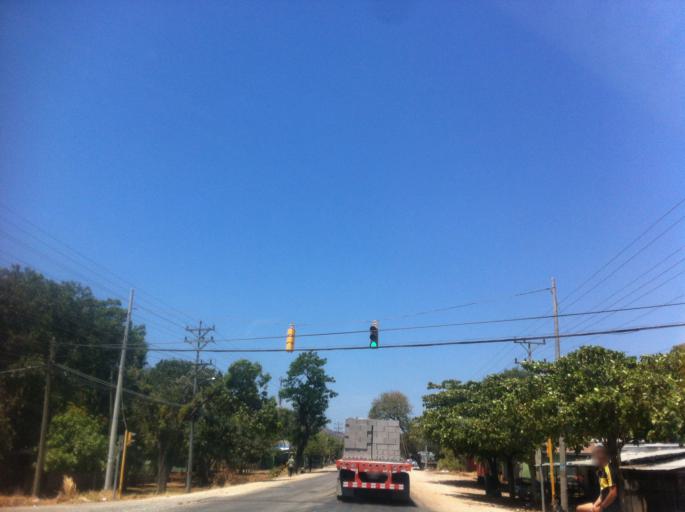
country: CR
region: Guanacaste
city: Santa Cruz
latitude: 10.2683
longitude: -85.5824
